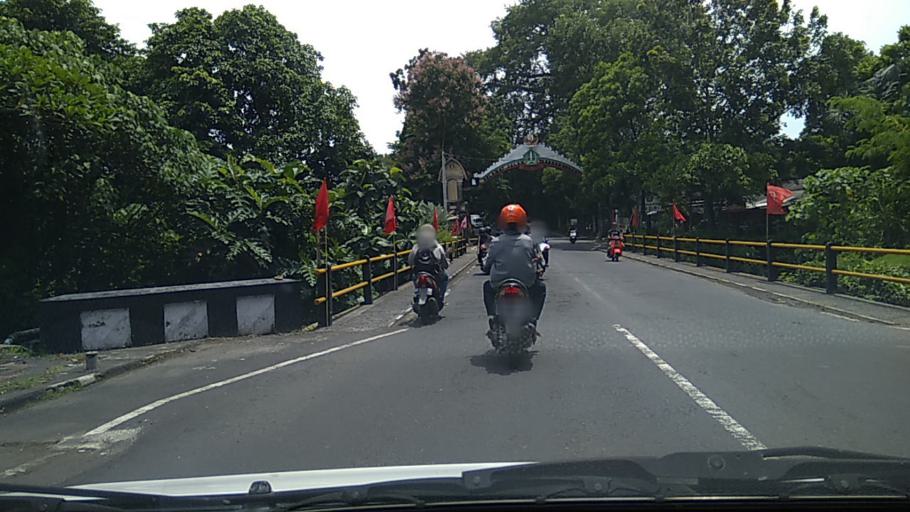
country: ID
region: Bali
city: Tabanan
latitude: -8.5411
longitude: 115.1378
